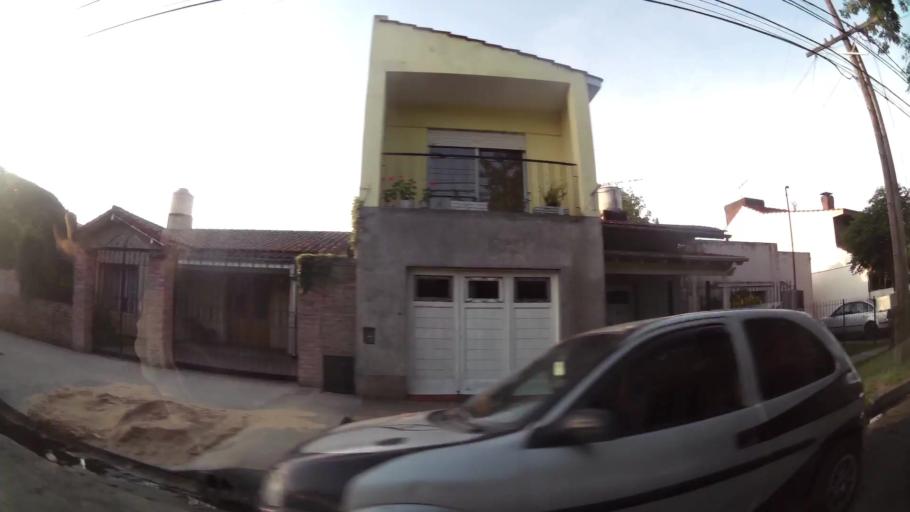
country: AR
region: Buenos Aires
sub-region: Partido de Tigre
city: Tigre
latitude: -34.4583
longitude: -58.6334
